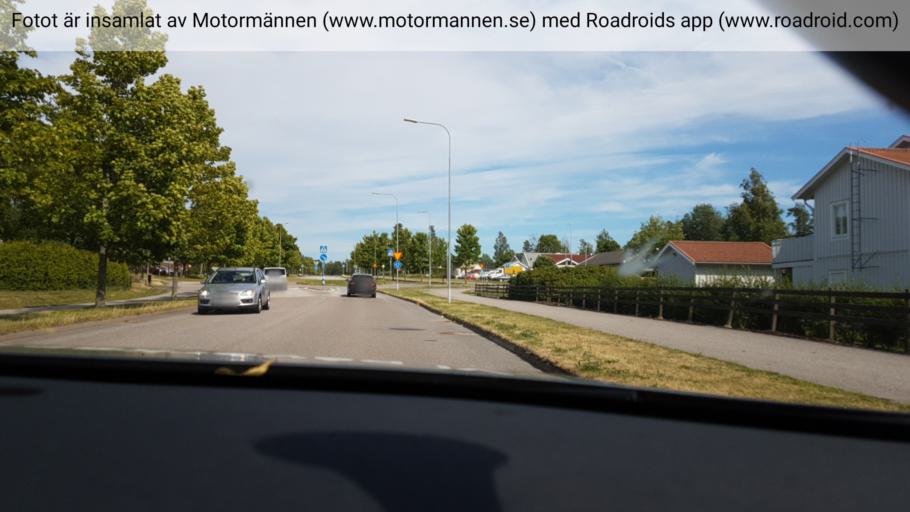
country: SE
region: Vaestra Goetaland
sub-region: Mariestads Kommun
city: Mariestad
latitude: 58.7153
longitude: 13.8523
